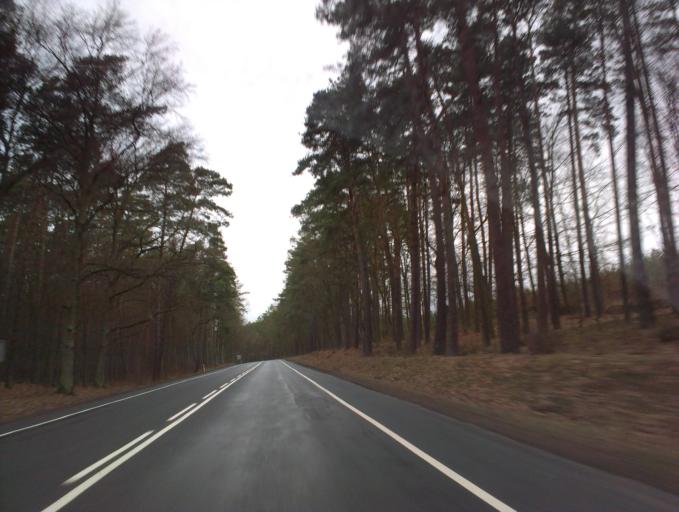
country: PL
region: Greater Poland Voivodeship
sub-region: Powiat chodzieski
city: Chodziez
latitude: 53.0009
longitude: 16.8658
